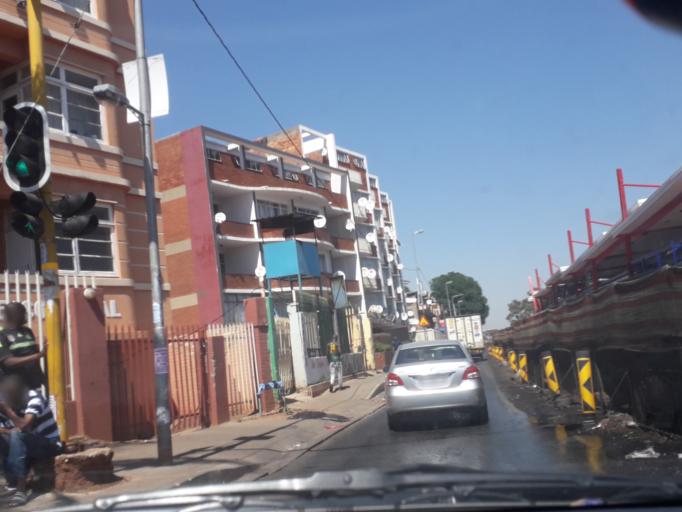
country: ZA
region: Gauteng
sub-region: City of Johannesburg Metropolitan Municipality
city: Johannesburg
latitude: -26.1783
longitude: 28.0595
